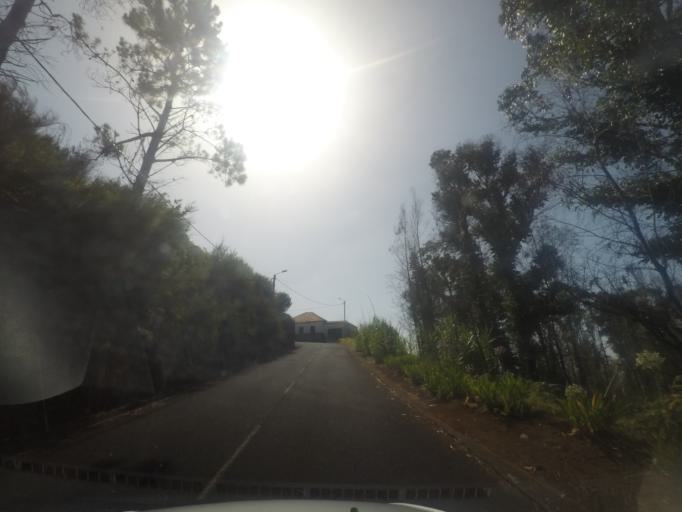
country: PT
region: Madeira
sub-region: Calheta
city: Faja da Ovelha
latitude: 32.8278
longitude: -17.2327
